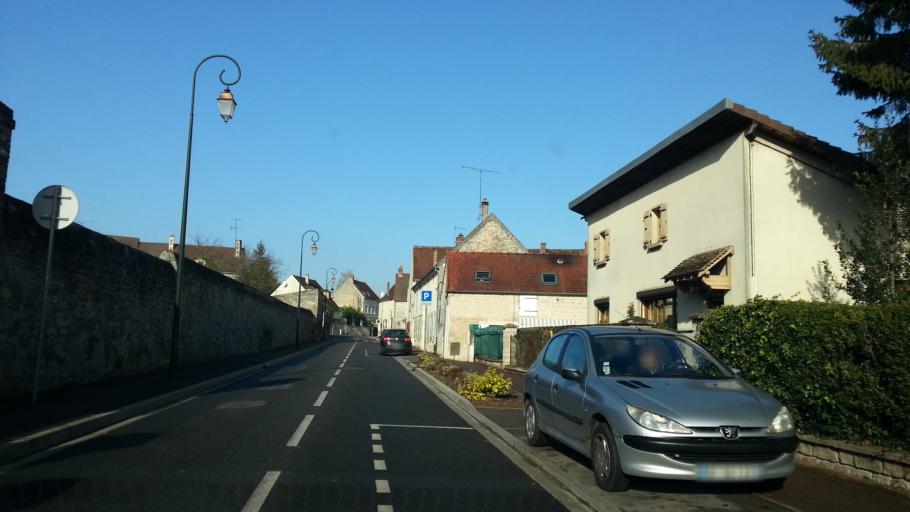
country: FR
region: Picardie
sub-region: Departement de l'Oise
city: Balagny-sur-Therain
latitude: 49.2929
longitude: 2.3380
